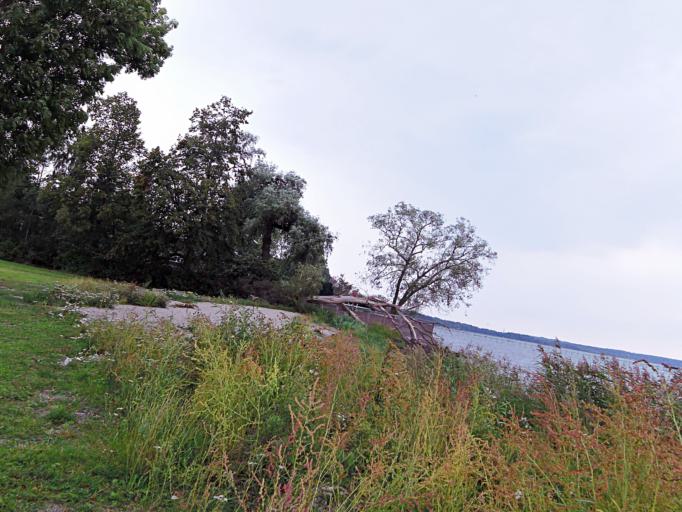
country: DK
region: Capital Region
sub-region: Fredensborg Kommune
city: Kokkedal
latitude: 55.9118
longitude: 12.5242
